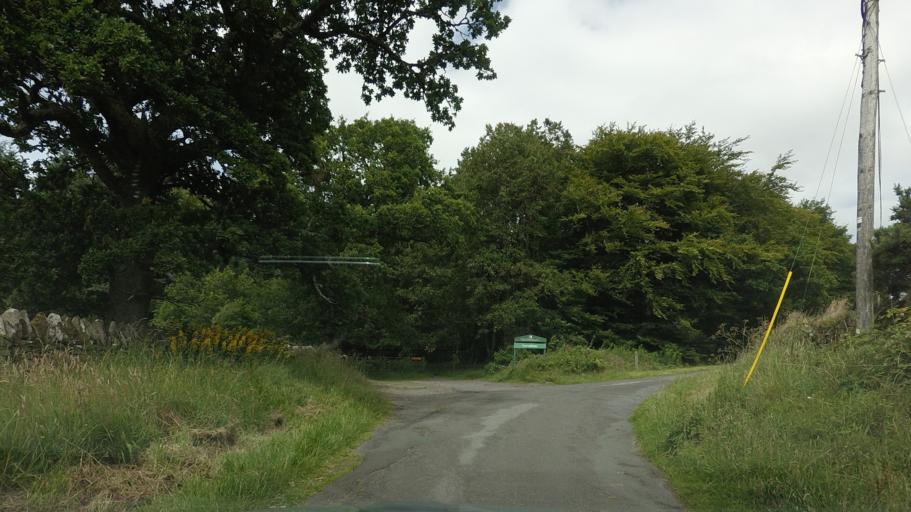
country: GB
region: Scotland
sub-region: Stirling
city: Killearn
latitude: 56.0817
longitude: -4.4497
